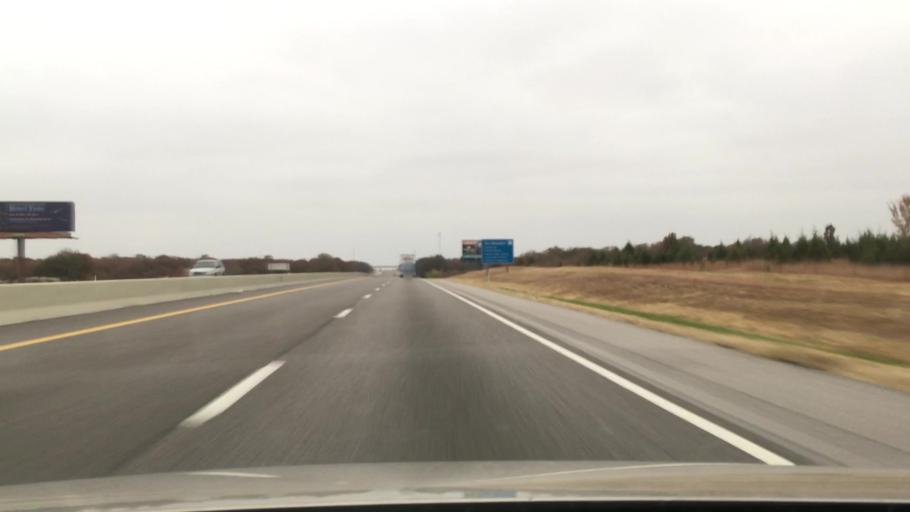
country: US
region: Oklahoma
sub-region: Lincoln County
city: Chandler
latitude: 35.7251
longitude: -96.8534
